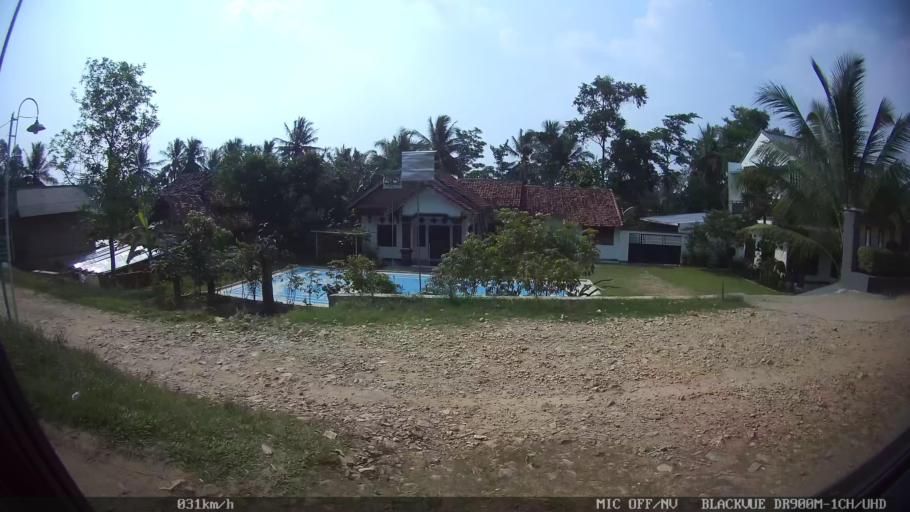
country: ID
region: Lampung
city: Pringsewu
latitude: -5.3827
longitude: 104.9951
